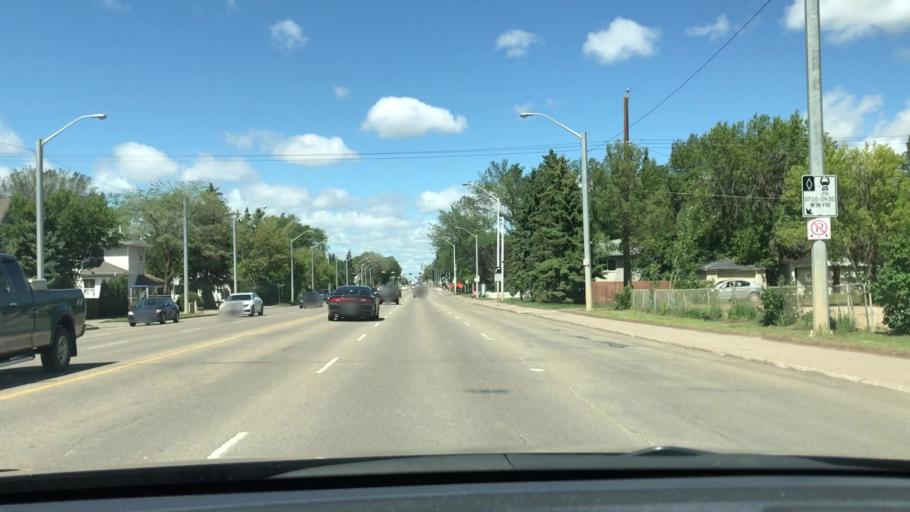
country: CA
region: Alberta
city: Edmonton
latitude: 53.5094
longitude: -113.5120
